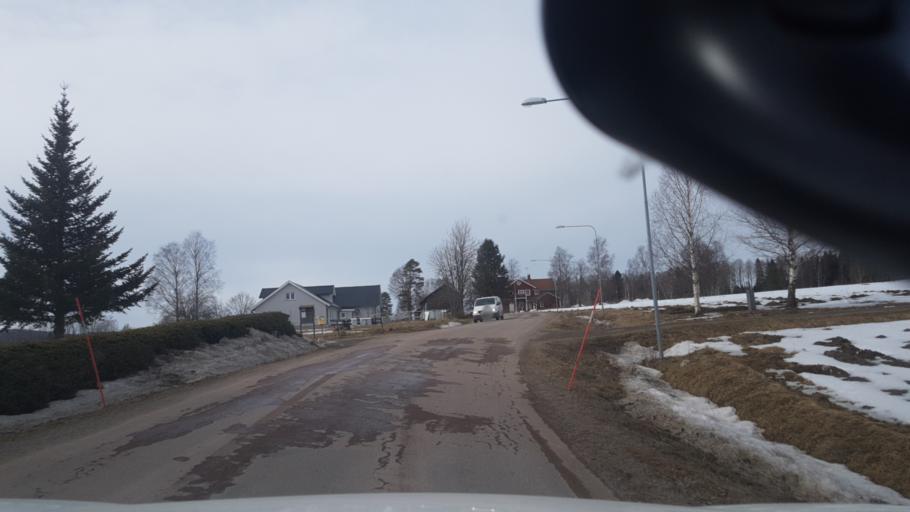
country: SE
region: Vaermland
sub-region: Eda Kommun
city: Charlottenberg
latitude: 59.8301
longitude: 12.3338
